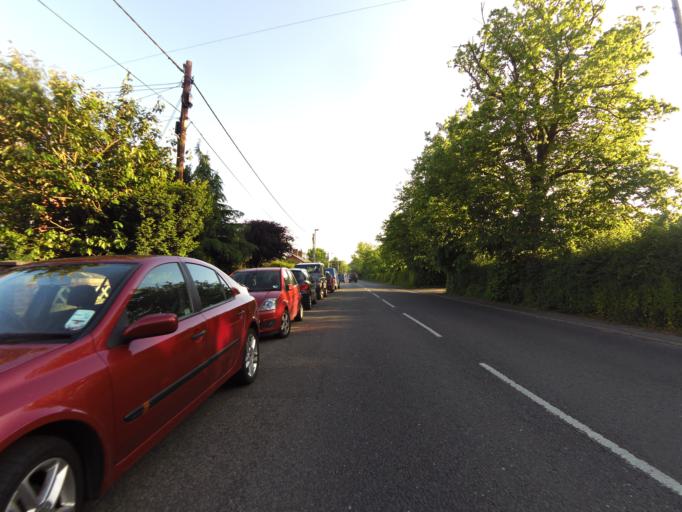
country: GB
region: England
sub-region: Suffolk
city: Woodbridge
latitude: 52.1029
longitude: 1.3279
